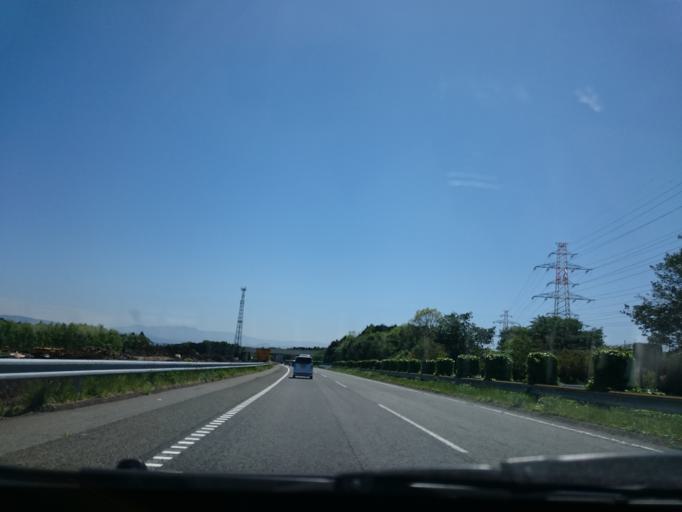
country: JP
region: Shizuoka
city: Gotemba
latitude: 35.2402
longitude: 138.9084
